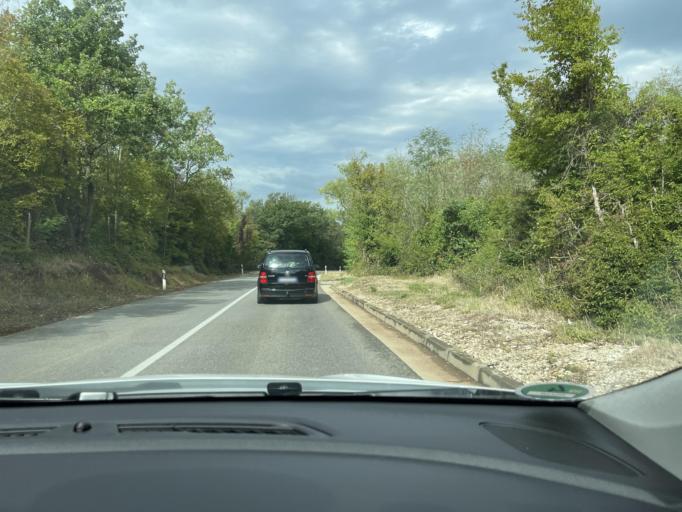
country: HR
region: Istarska
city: Vrsar
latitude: 45.2019
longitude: 13.6968
